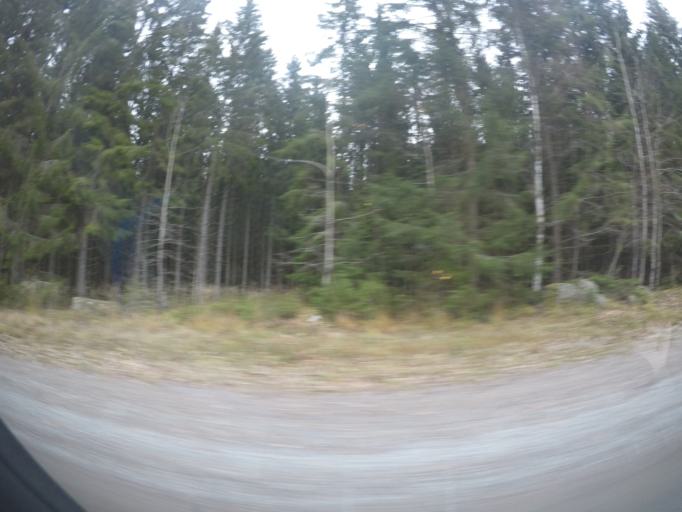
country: SE
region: Vaestmanland
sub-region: Surahammars Kommun
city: Ramnas
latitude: 59.7103
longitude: 16.0924
